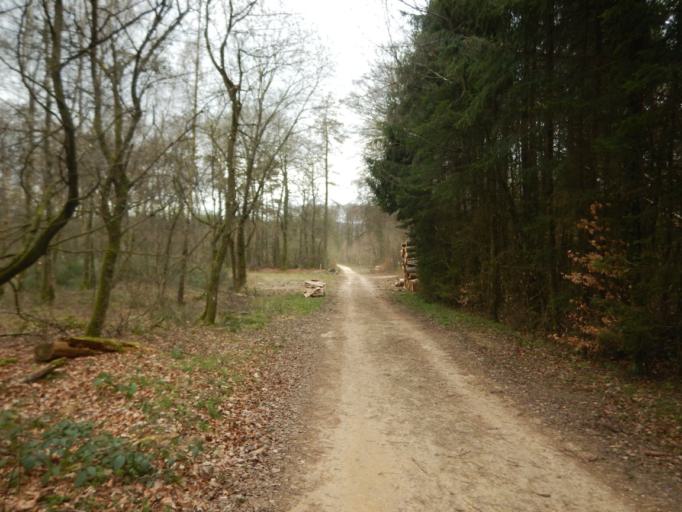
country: LU
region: Luxembourg
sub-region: Canton de Mersch
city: Lorentzweiler
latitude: 49.6951
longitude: 6.1610
